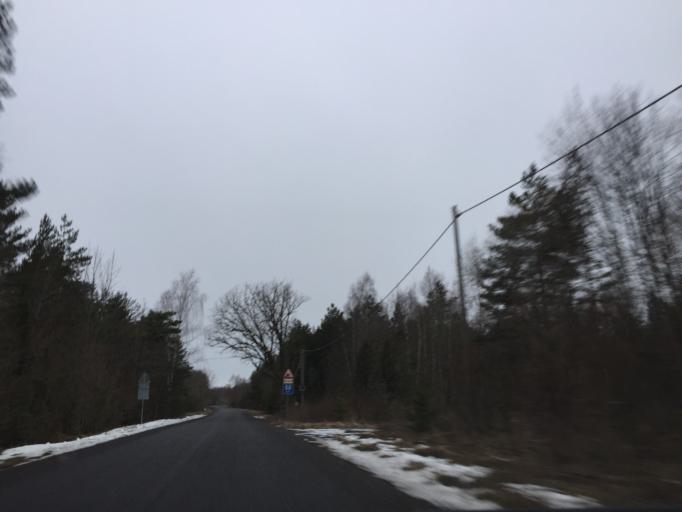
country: EE
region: Laeaene
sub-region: Lihula vald
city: Lihula
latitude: 58.6595
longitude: 23.5803
